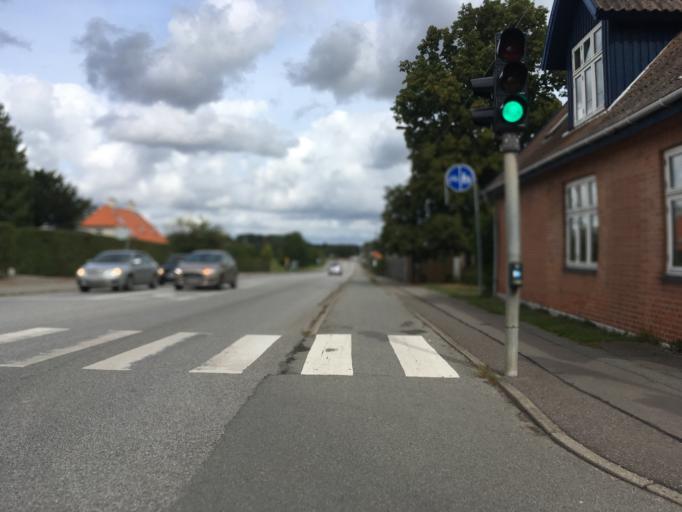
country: DK
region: Capital Region
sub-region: Hillerod Kommune
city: Hillerod
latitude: 55.9158
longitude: 12.2882
